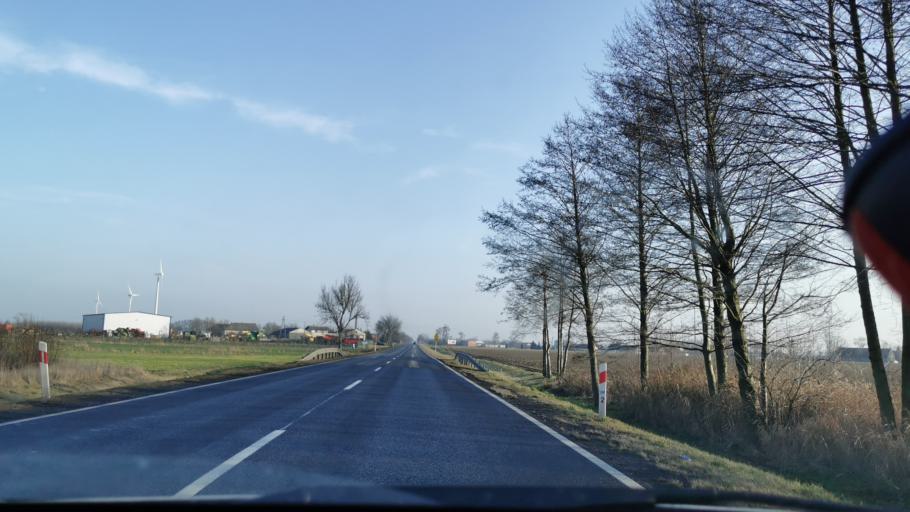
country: PL
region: Lodz Voivodeship
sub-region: Powiat sieradzki
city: Blaszki
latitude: 51.6690
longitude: 18.3778
